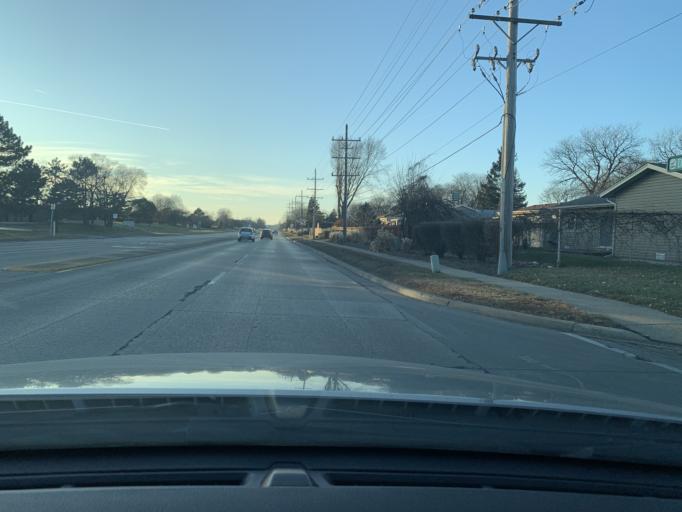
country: US
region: Illinois
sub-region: DuPage County
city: Itasca
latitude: 41.9927
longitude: -88.0058
